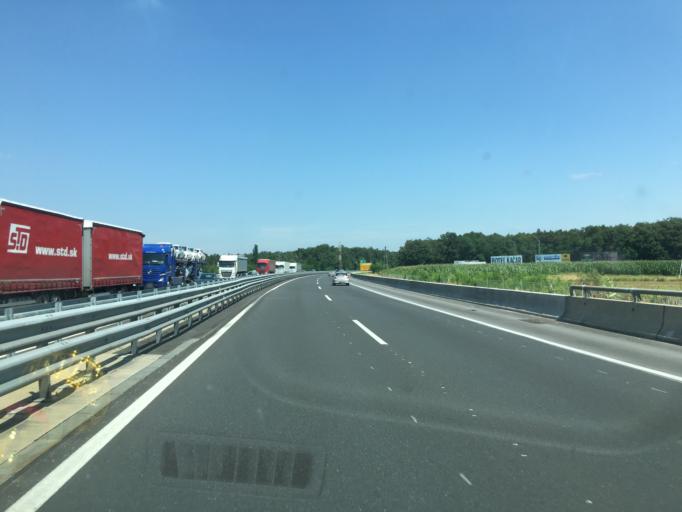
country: SI
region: Hoce-Slivnica
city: Rogoza
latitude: 46.5095
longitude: 15.6696
